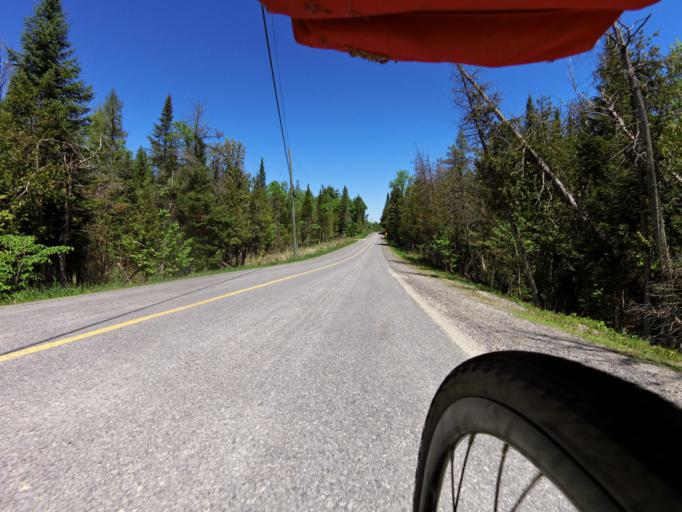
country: CA
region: Ontario
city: Carleton Place
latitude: 45.1771
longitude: -76.4052
